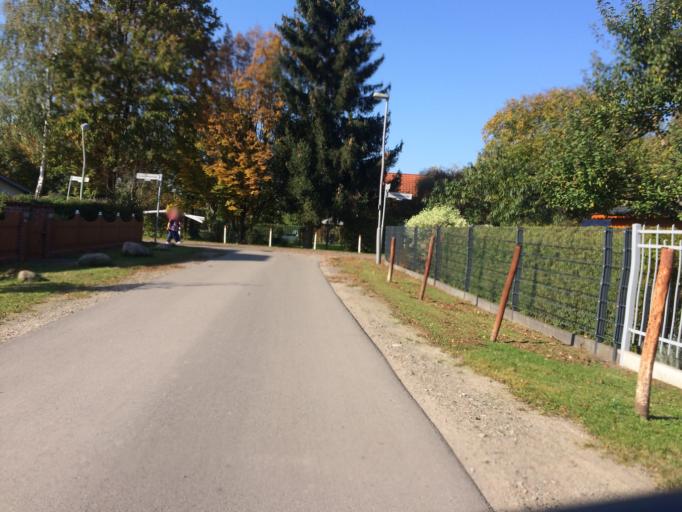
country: DE
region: Berlin
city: Buchholz
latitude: 52.6101
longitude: 13.4437
